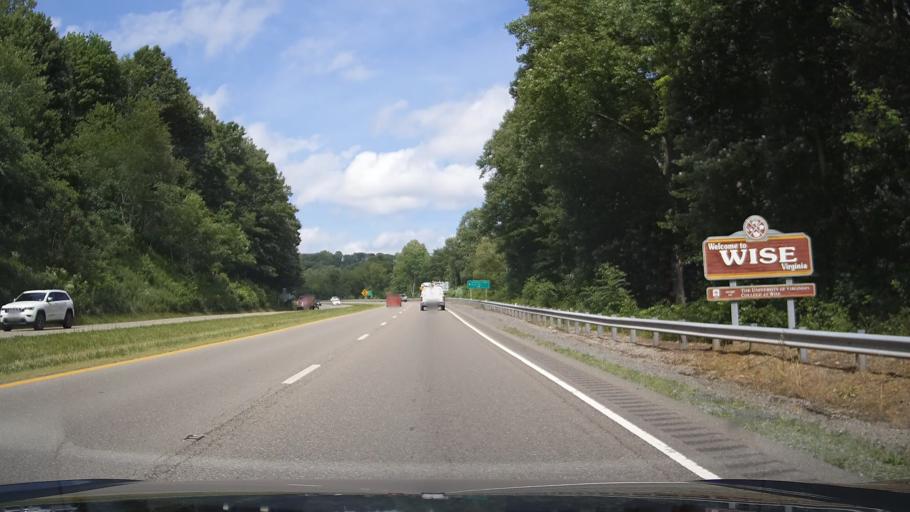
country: US
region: Virginia
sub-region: Wise County
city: Wise
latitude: 36.9649
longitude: -82.5988
